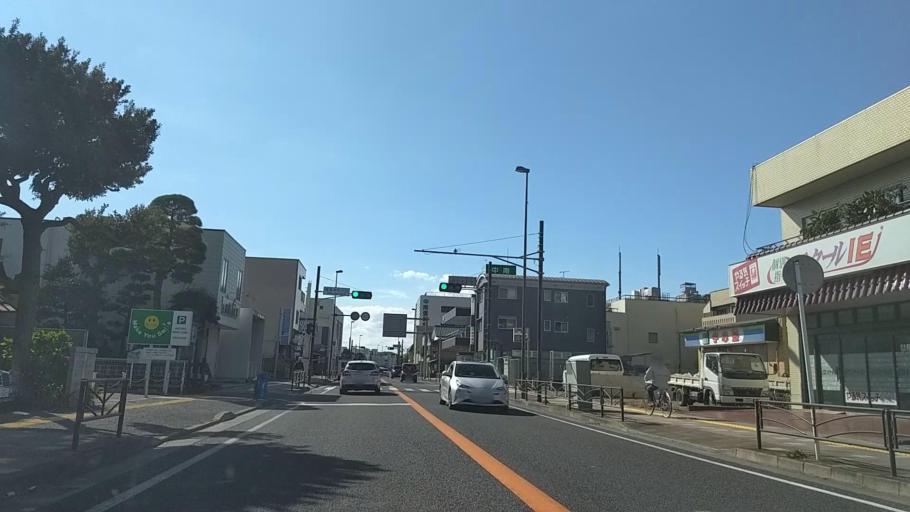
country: JP
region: Kanagawa
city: Oiso
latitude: 35.3100
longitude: 139.3159
